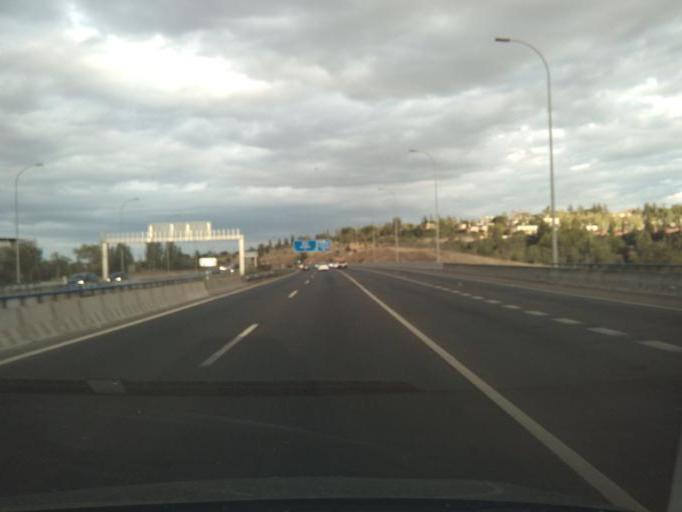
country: ES
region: Madrid
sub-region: Provincia de Madrid
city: Alcobendas
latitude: 40.5323
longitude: -3.6312
